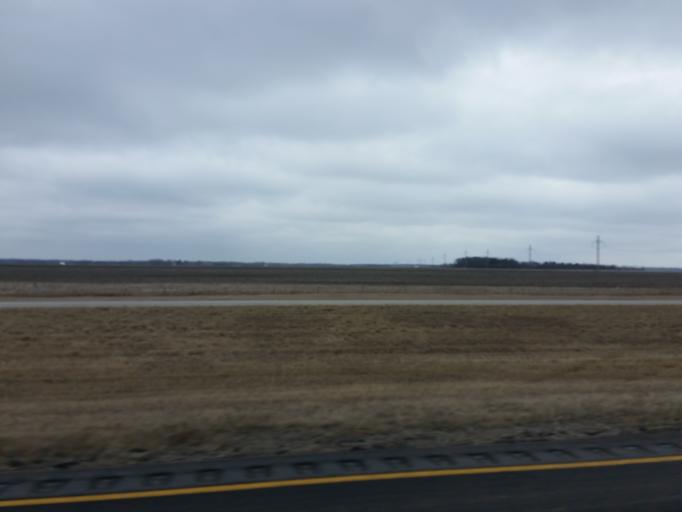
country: US
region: North Dakota
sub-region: Cass County
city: Horace
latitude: 46.6245
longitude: -96.8309
